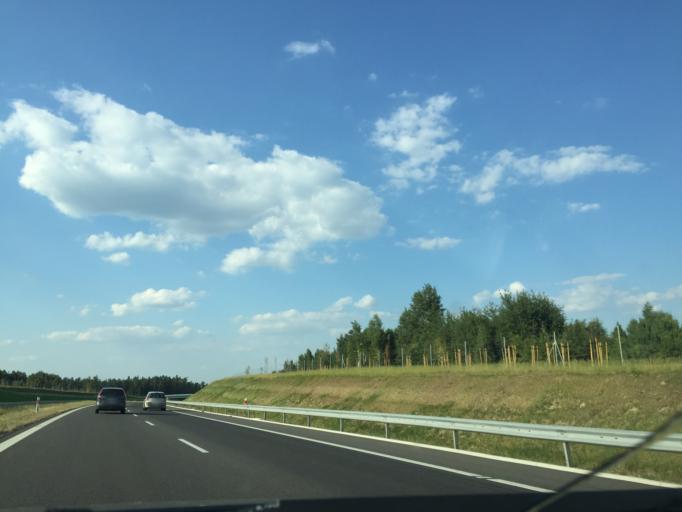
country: PL
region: Swietokrzyskie
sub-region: Powiat skarzyski
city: Skarzysko-Kamienna
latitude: 51.1389
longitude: 20.8324
